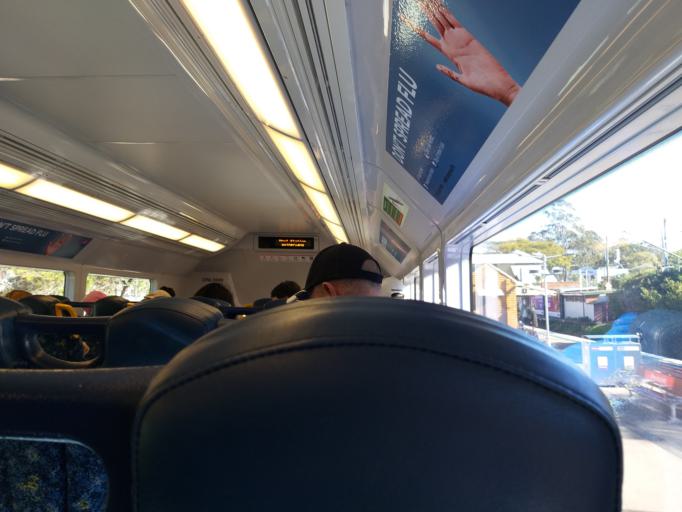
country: AU
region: New South Wales
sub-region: Hurstville
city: Penshurst
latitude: -33.9658
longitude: 151.0914
